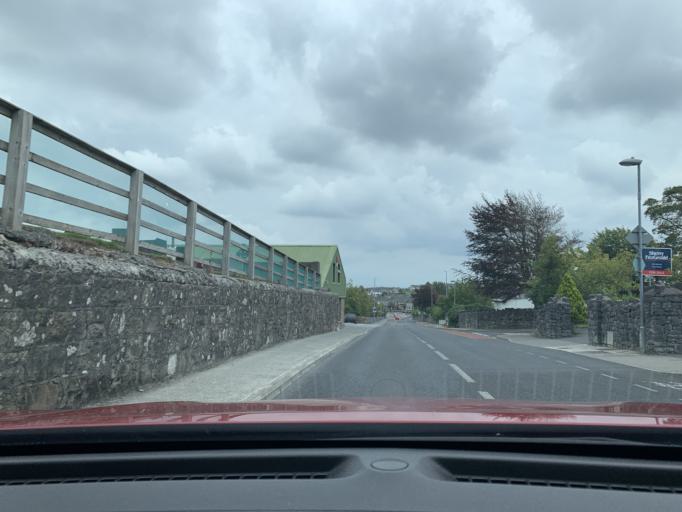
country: IE
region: Connaught
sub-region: County Galway
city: Gaillimh
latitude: 53.2748
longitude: -9.0898
